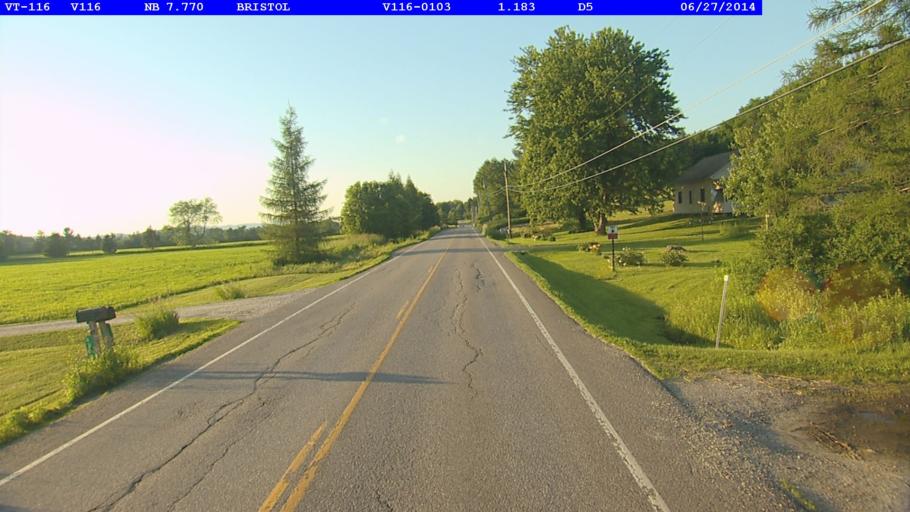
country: US
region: Vermont
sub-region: Addison County
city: Bristol
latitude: 44.0708
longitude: -73.0860
